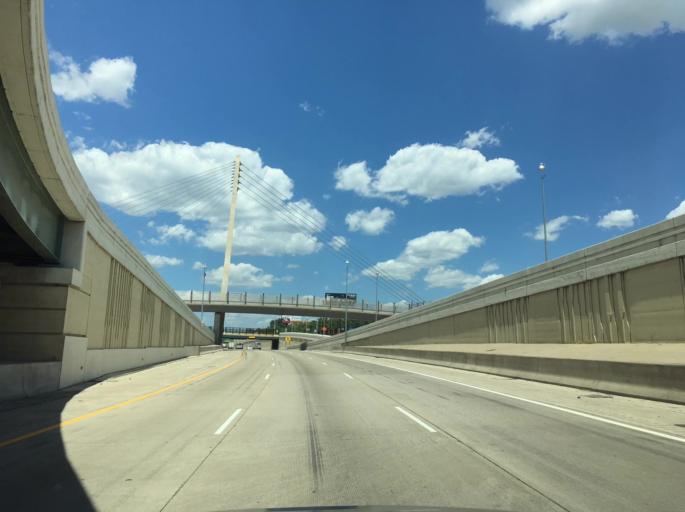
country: US
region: Michigan
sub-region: Wayne County
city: Detroit
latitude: 42.3230
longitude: -83.0823
